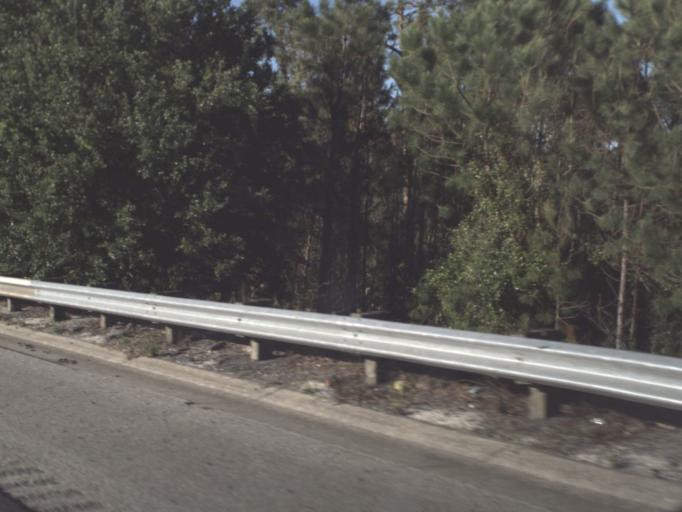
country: US
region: Florida
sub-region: Flagler County
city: Flagler Beach
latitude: 29.4993
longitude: -81.1925
